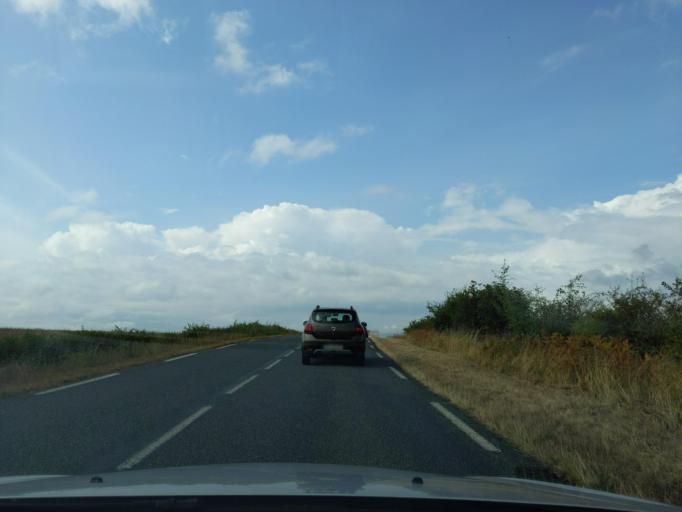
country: FR
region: Bourgogne
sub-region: Departement de Saone-et-Loire
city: Bourbon-Lancy
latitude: 46.6602
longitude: 3.7990
